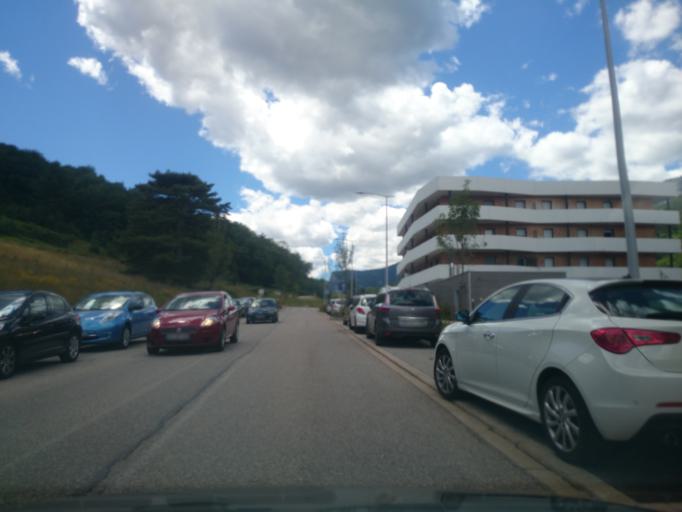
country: FR
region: Rhone-Alpes
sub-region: Departement de l'Isere
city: Seyssins
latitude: 45.1521
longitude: 5.6825
